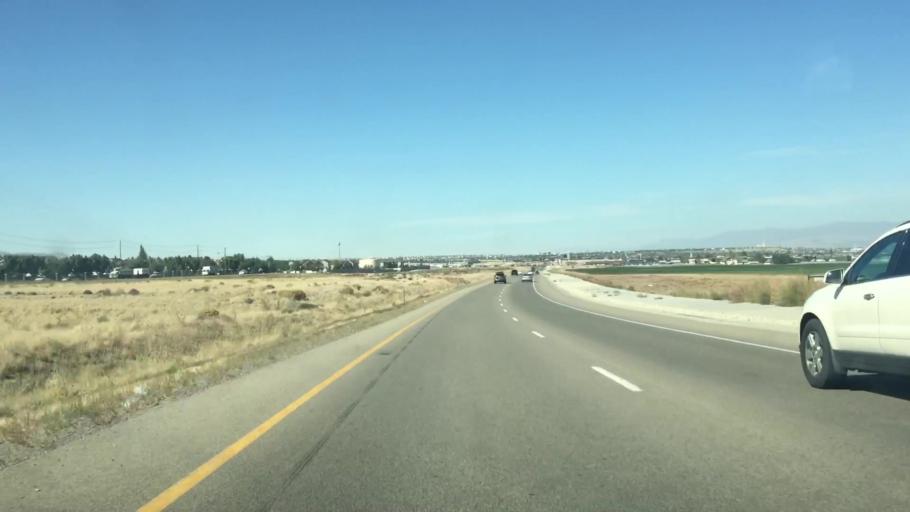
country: US
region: Utah
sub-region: Salt Lake County
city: Herriman
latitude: 40.4957
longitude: -112.0017
